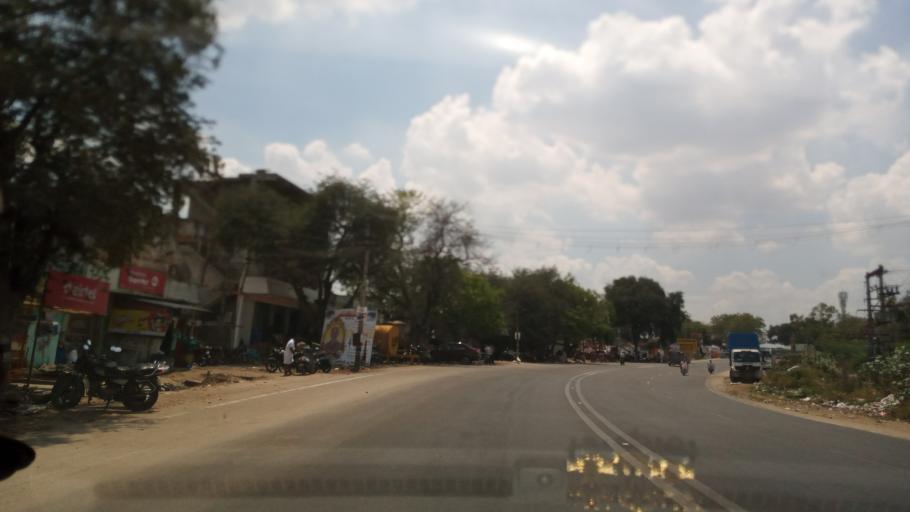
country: IN
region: Tamil Nadu
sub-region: Vellore
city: Walajapet
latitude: 12.9255
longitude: 79.3525
